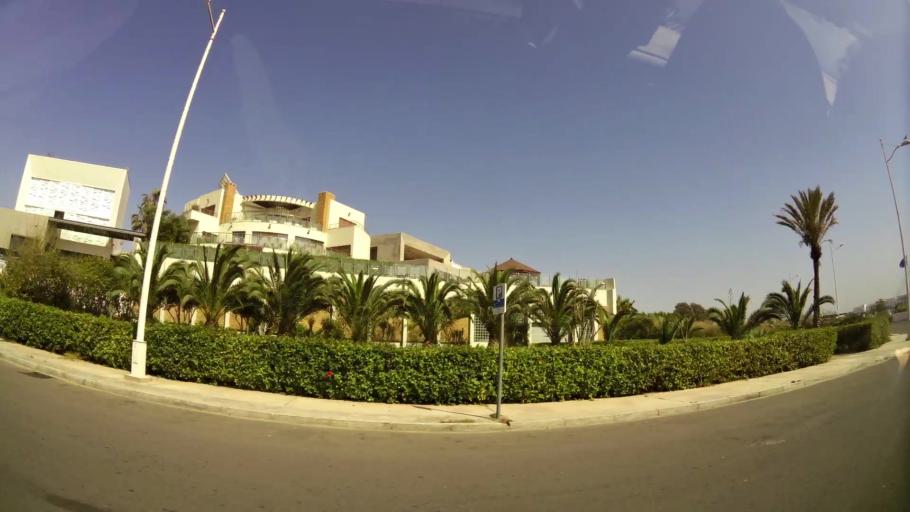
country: MA
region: Souss-Massa-Draa
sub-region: Agadir-Ida-ou-Tnan
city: Agadir
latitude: 30.3921
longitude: -9.5964
